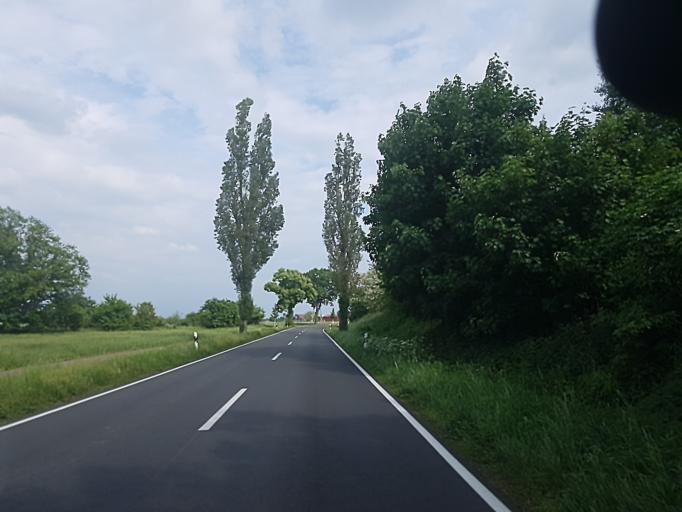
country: DE
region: Saxony-Anhalt
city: Coswig
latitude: 51.8983
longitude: 12.4414
